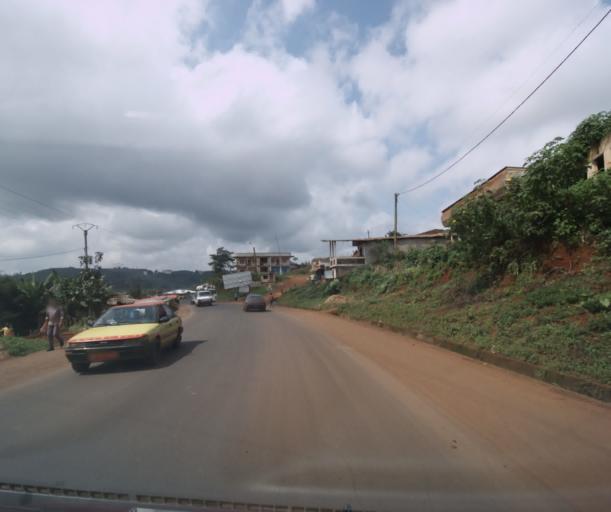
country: CM
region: West
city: Dschang
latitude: 5.4564
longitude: 10.0686
